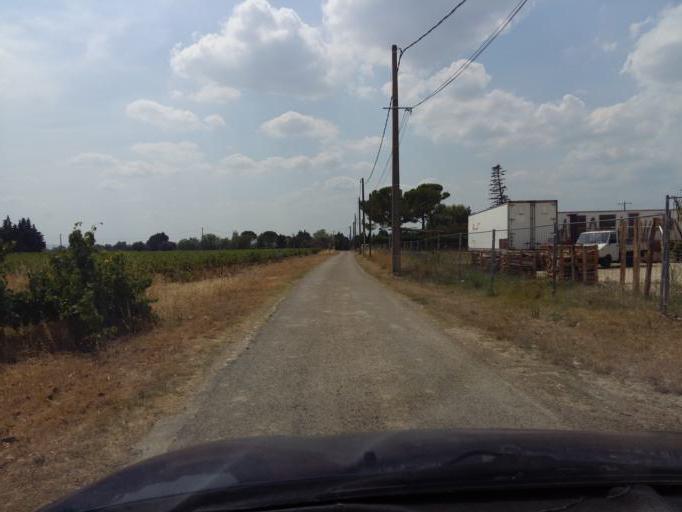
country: FR
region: Provence-Alpes-Cote d'Azur
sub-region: Departement du Vaucluse
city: Piolenc
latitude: 44.1621
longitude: 4.7865
